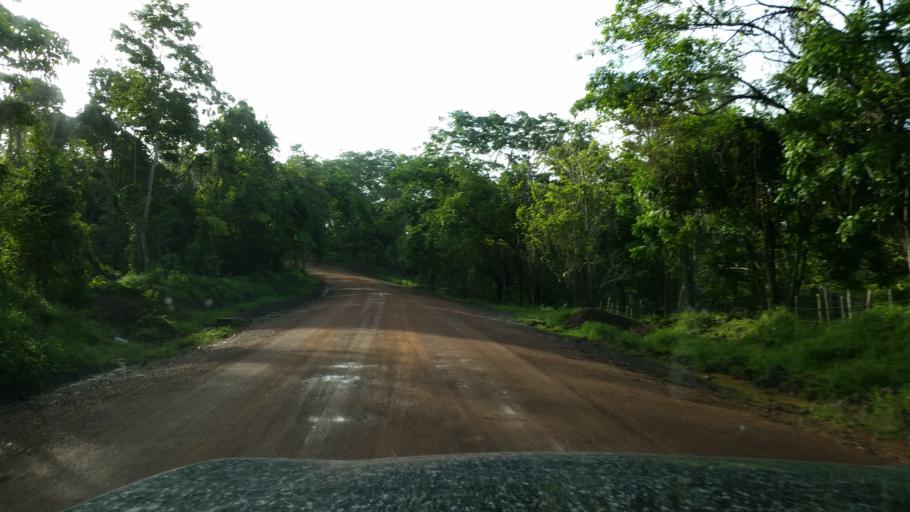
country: NI
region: Atlantico Norte (RAAN)
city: Puerto Cabezas
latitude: 14.0674
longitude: -83.9732
